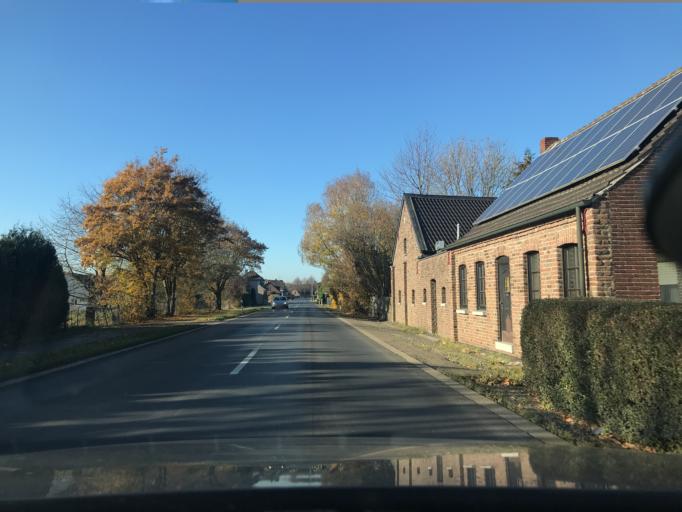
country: DE
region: North Rhine-Westphalia
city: Kempen
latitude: 51.3917
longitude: 6.4275
